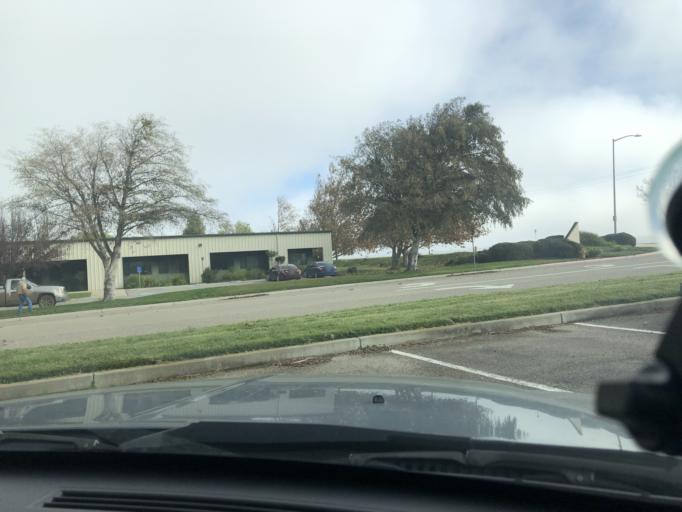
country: US
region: California
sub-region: Monterey County
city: King City
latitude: 36.2207
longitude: -121.1205
